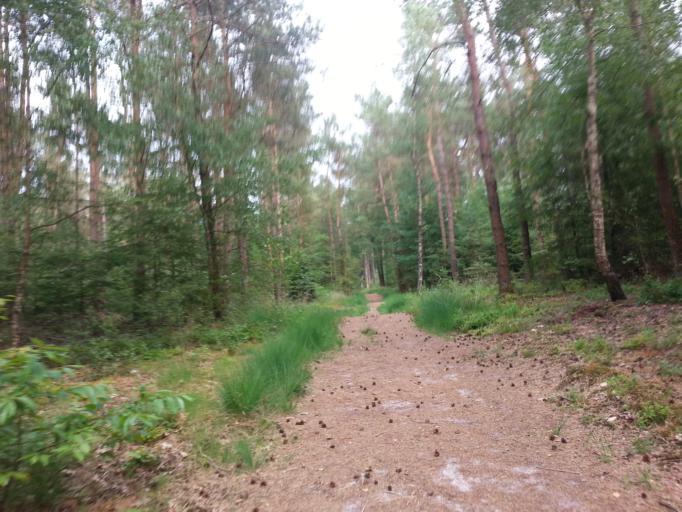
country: NL
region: Utrecht
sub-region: Gemeente Amersfoort
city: Randenbroek
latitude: 52.1109
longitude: 5.3803
